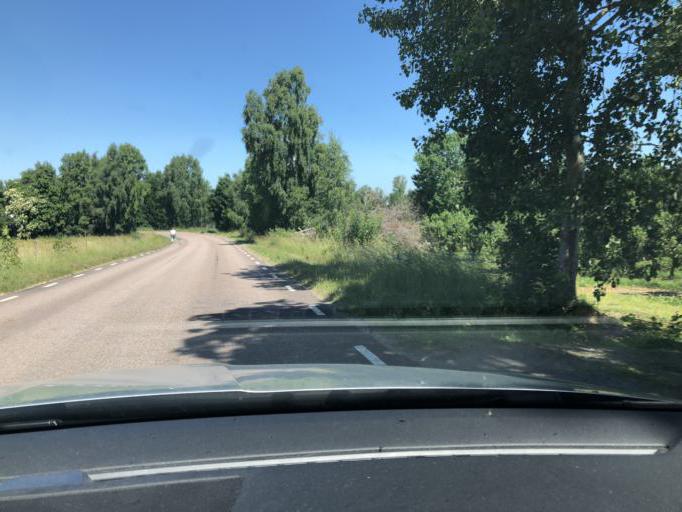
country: SE
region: Blekinge
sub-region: Solvesborgs Kommun
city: Soelvesborg
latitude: 56.1565
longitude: 14.6010
